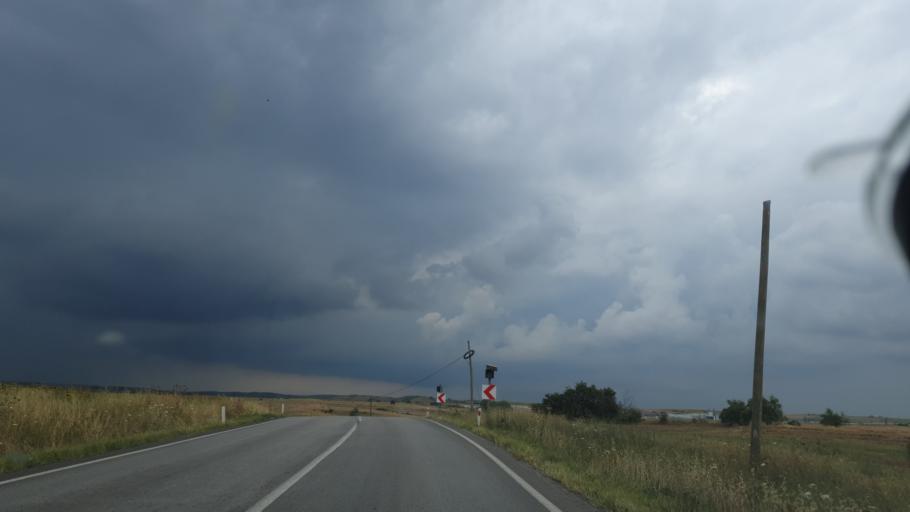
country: TR
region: Tekirdag
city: Hayrabolu
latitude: 41.2203
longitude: 27.0681
